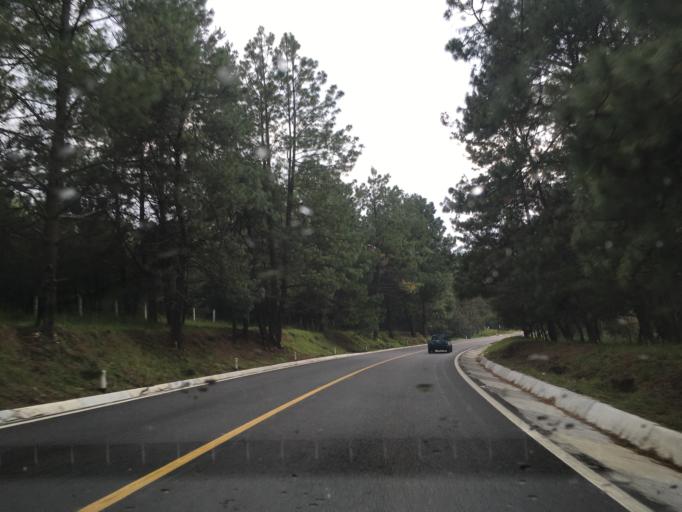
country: MX
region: Michoacan
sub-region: Patzcuaro
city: Santa Maria Huiramangaro (San Juan Tumbio)
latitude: 19.4901
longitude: -101.7823
